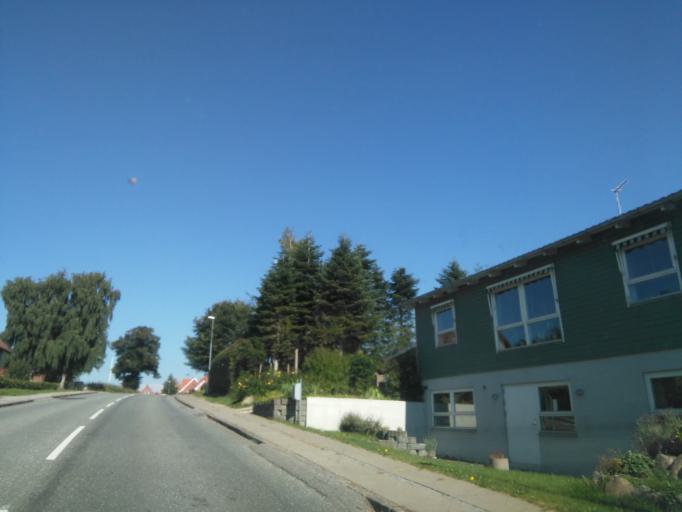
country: DK
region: Central Jutland
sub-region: Syddjurs Kommune
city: Ronde
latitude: 56.2453
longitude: 10.4940
